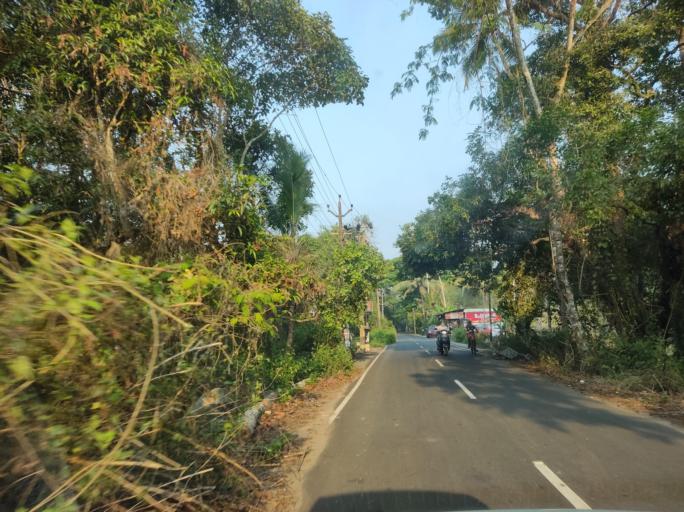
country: IN
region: Kerala
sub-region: Alappuzha
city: Alleppey
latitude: 9.5907
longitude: 76.3119
